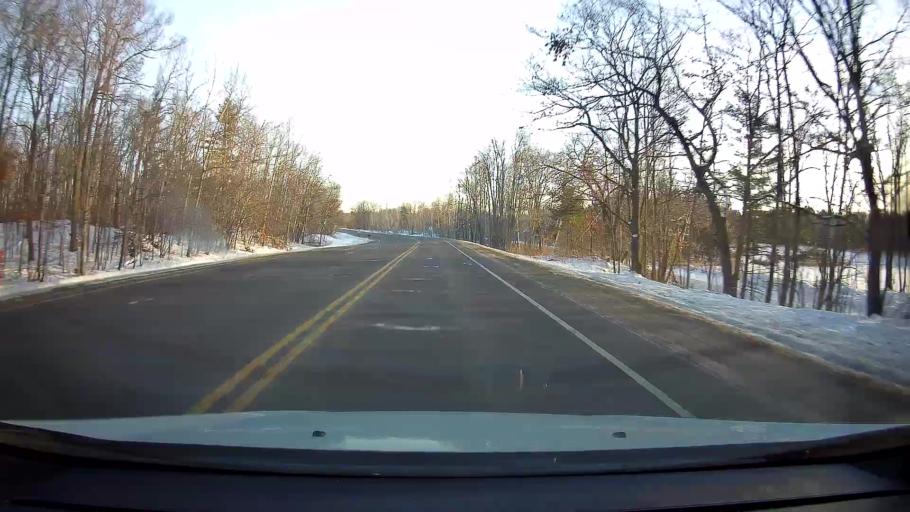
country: US
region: Wisconsin
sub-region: Barron County
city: Turtle Lake
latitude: 45.4481
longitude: -92.1101
